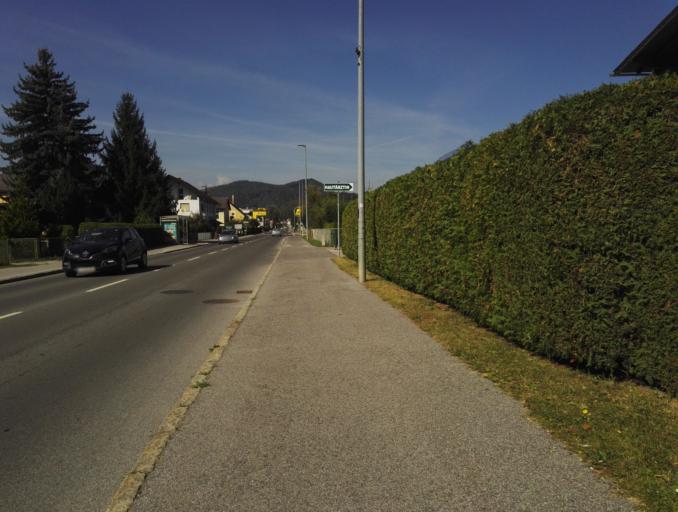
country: AT
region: Styria
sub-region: Politischer Bezirk Graz-Umgebung
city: Gratkorn
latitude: 47.1267
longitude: 15.3476
